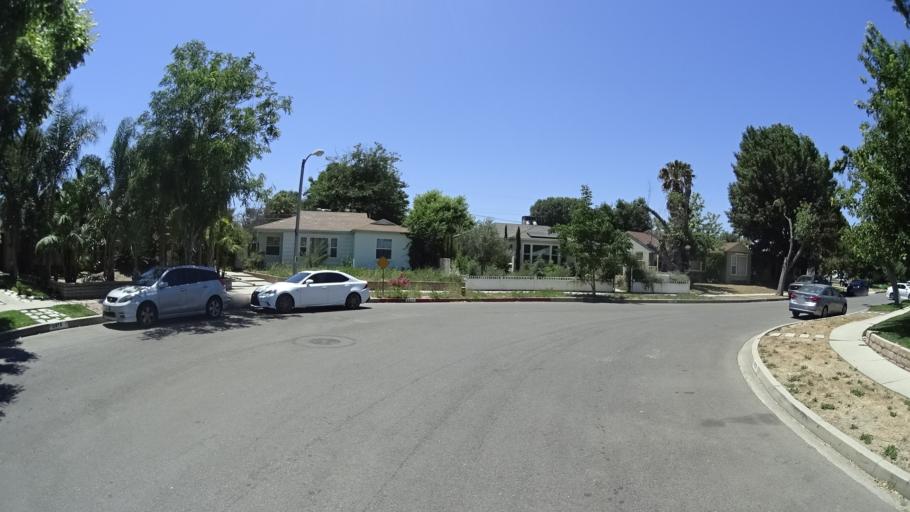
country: US
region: California
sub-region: Los Angeles County
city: Northridge
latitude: 34.1875
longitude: -118.5261
